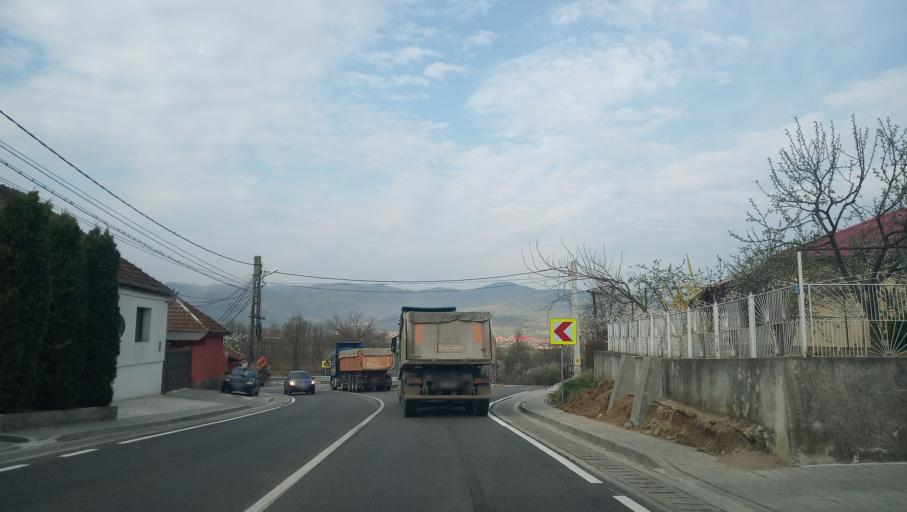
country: RO
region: Bihor
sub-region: Comuna Rieni
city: Ghighiseni
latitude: 46.5554
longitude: 22.4468
